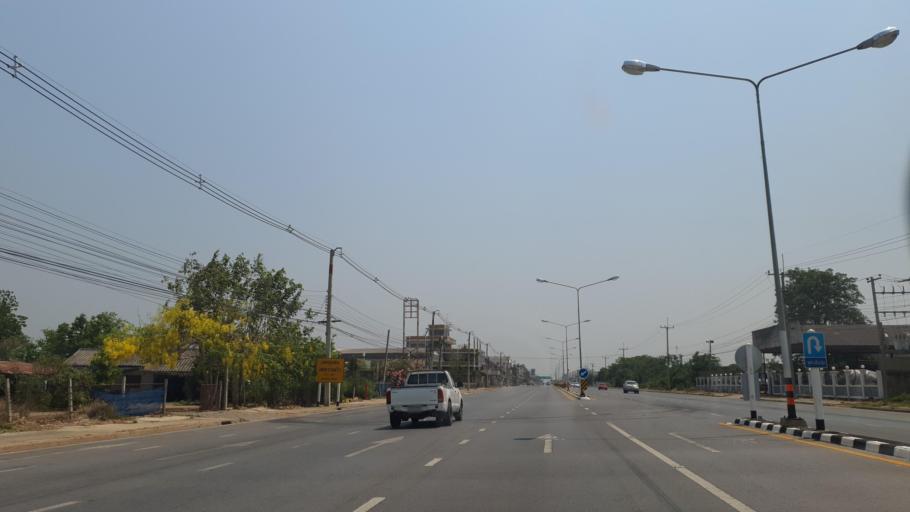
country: TH
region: Suphan Buri
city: U Thong
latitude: 14.2476
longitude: 99.8129
